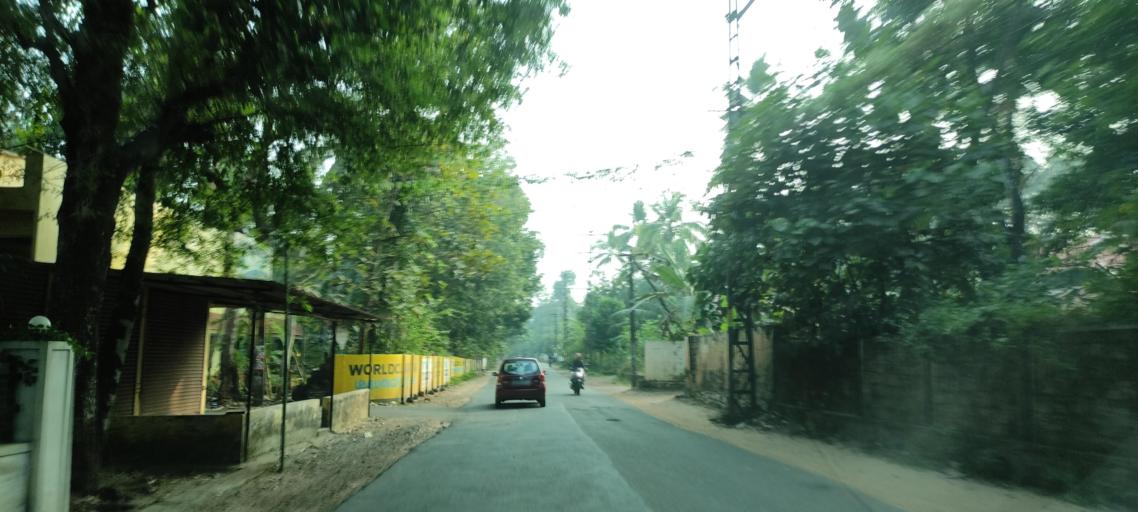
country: IN
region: Kerala
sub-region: Kottayam
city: Vaikam
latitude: 9.7121
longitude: 76.4757
